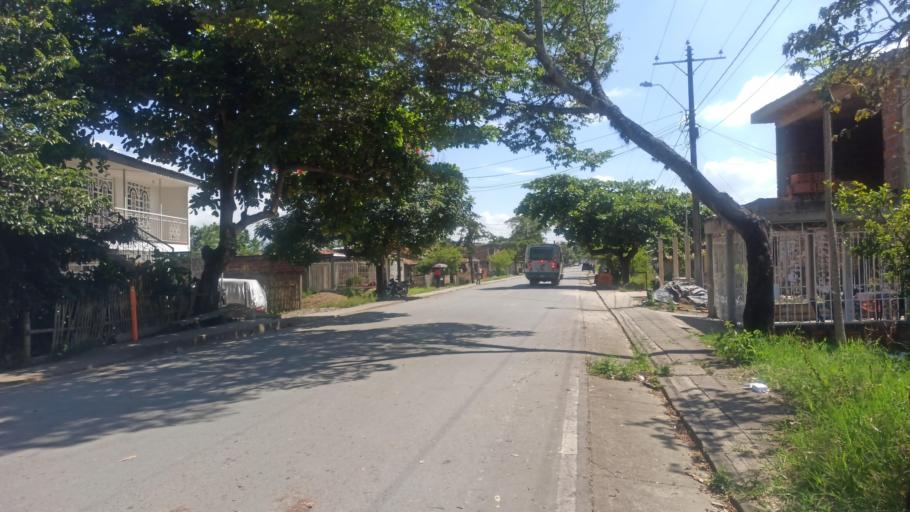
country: CO
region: Valle del Cauca
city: Jamundi
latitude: 3.1312
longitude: -76.5452
